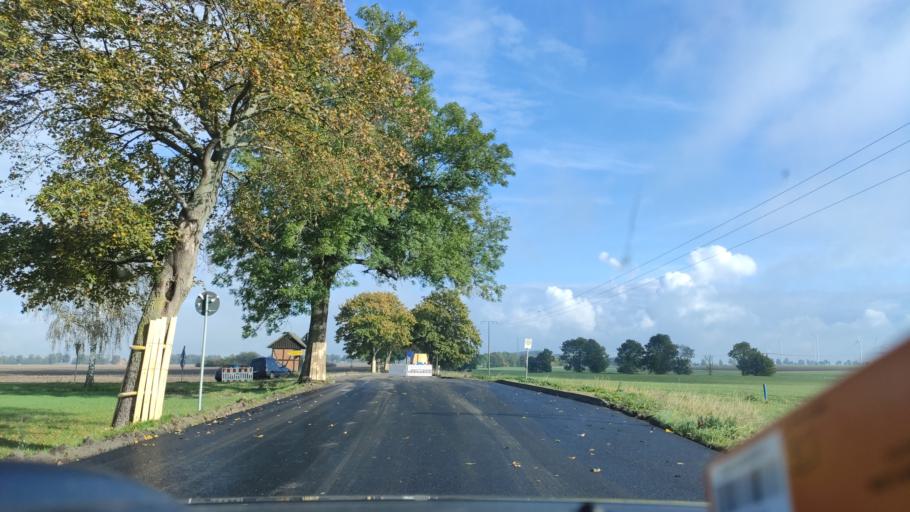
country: DE
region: Mecklenburg-Vorpommern
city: Dersekow
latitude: 54.0634
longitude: 13.1803
